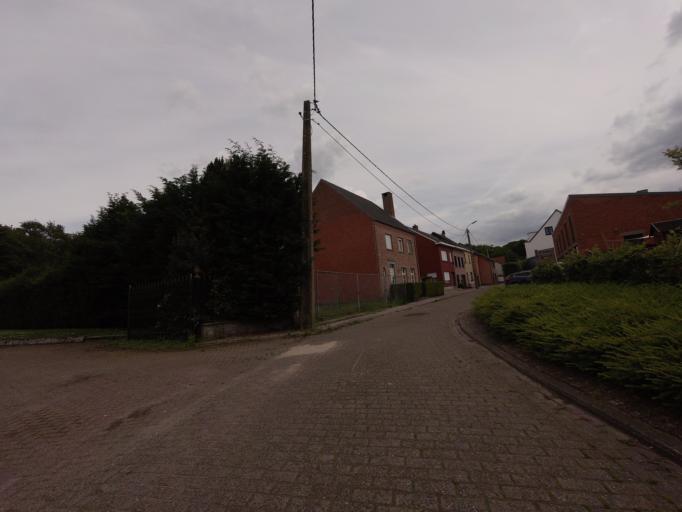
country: BE
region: Flanders
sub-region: Provincie Antwerpen
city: Bornem
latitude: 51.1079
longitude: 4.2689
